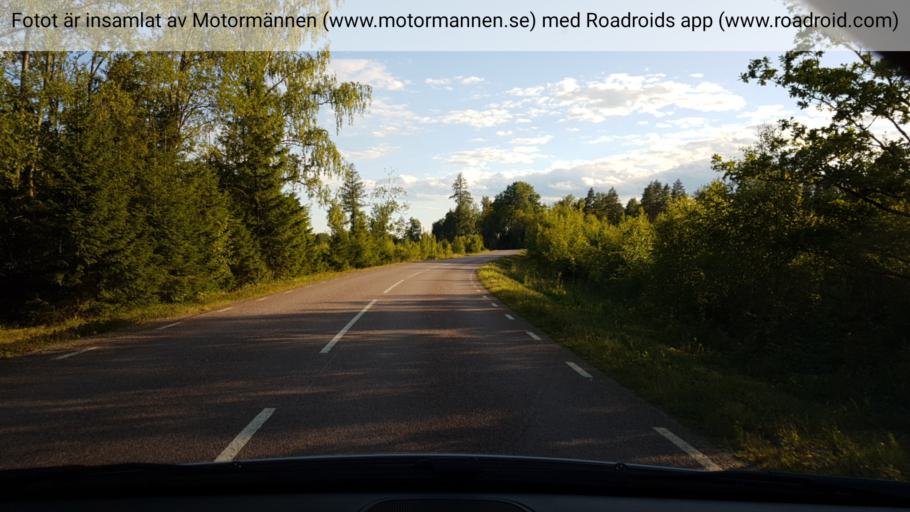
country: SE
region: Vaestmanland
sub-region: Vasteras
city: Tillberga
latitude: 59.7258
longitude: 16.6726
